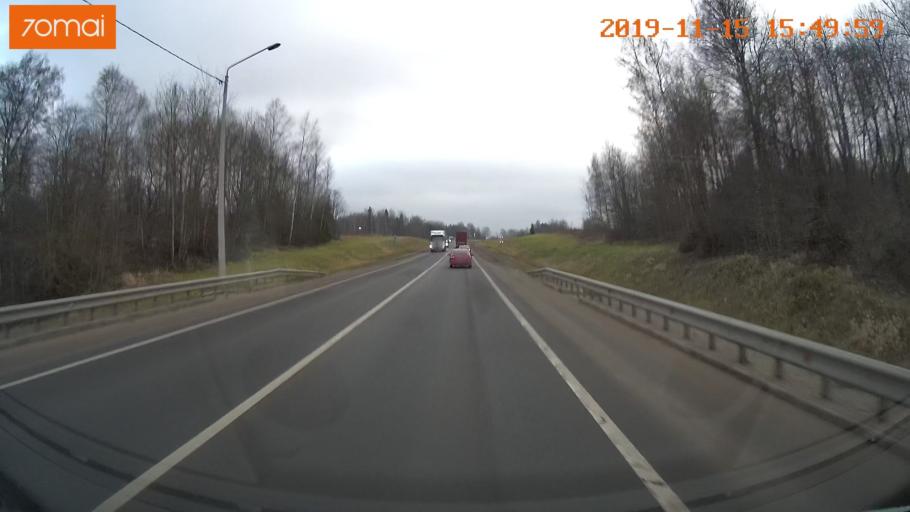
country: RU
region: Jaroslavl
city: Yaroslavl
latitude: 57.9103
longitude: 40.0117
